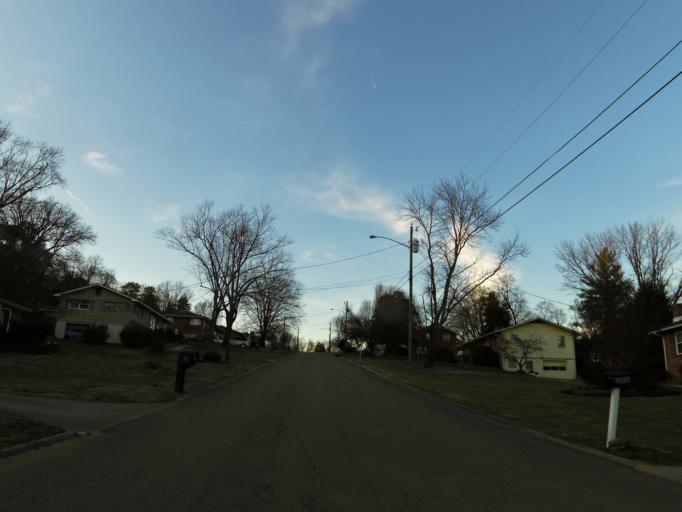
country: US
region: Tennessee
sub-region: Knox County
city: Knoxville
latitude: 36.0183
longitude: -83.8776
